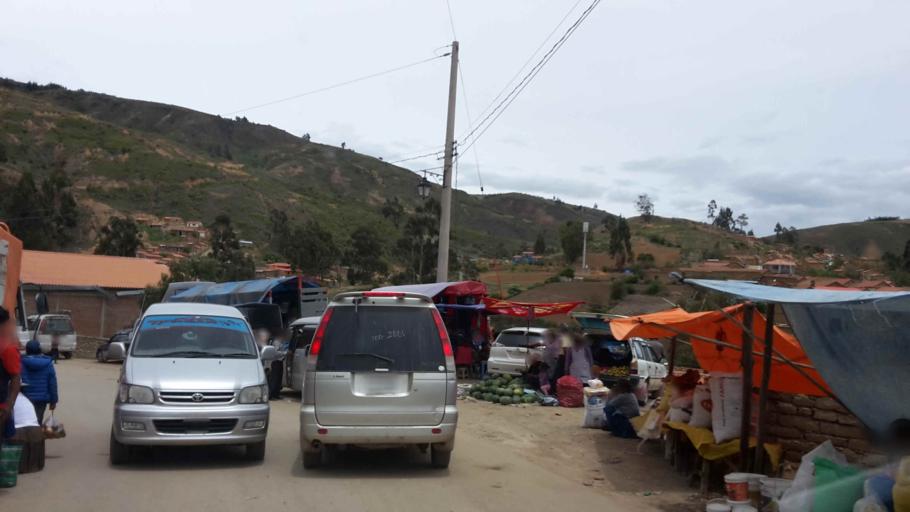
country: BO
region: Cochabamba
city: Totora
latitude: -17.7343
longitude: -65.1908
